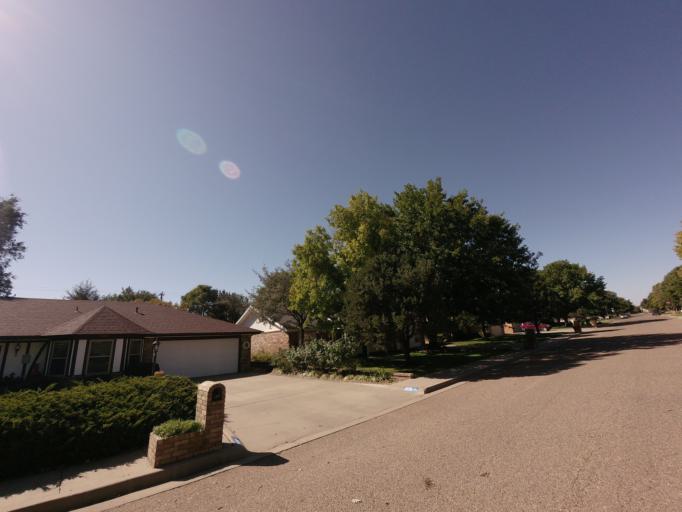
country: US
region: New Mexico
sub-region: Curry County
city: Clovis
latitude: 34.4207
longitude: -103.1732
